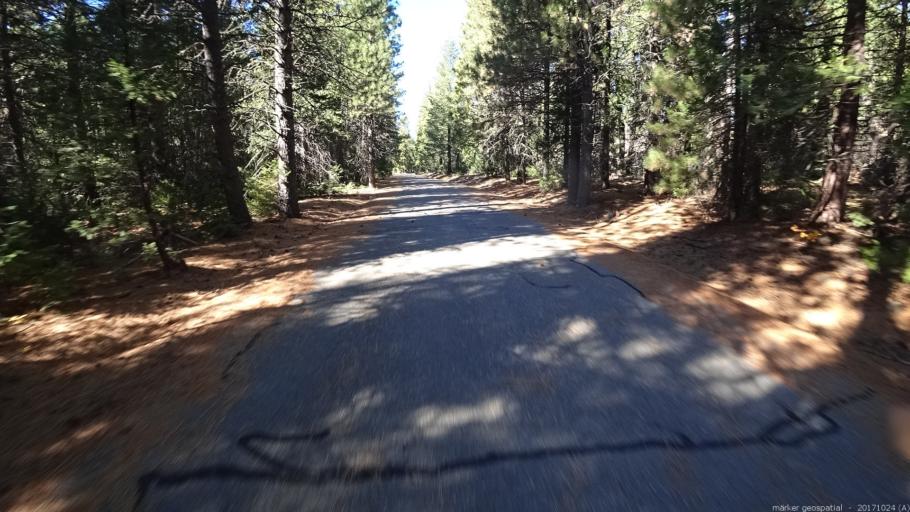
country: US
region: California
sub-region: Shasta County
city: Shingletown
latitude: 40.5019
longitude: -121.6604
